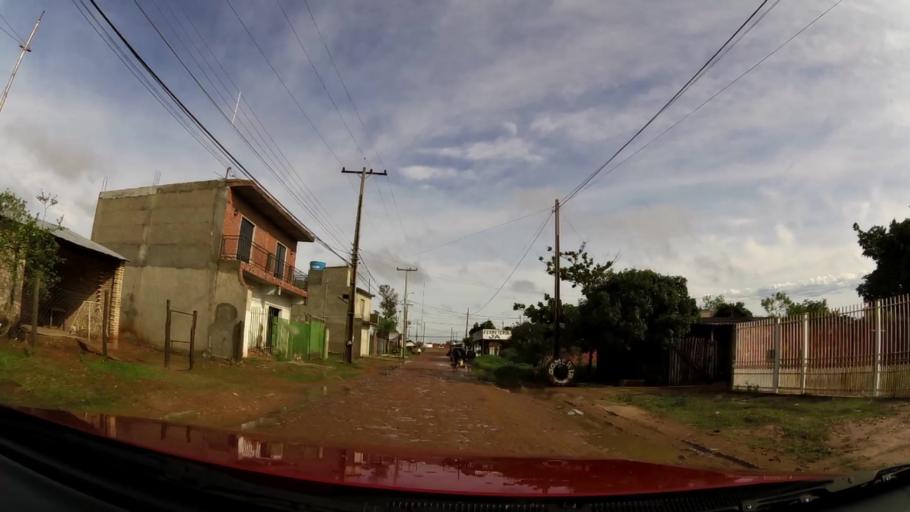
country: PY
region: Central
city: Limpio
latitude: -25.1825
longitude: -57.4899
